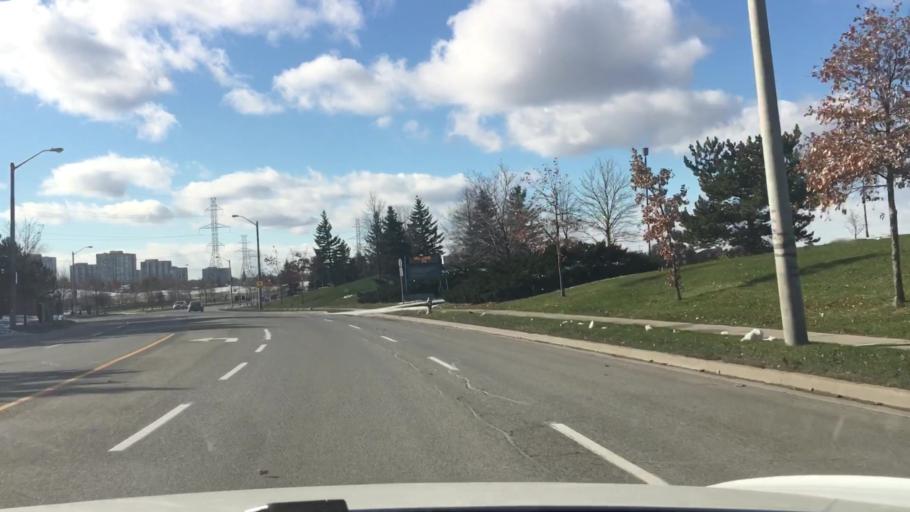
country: CA
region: Ontario
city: Scarborough
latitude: 43.8116
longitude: -79.3038
